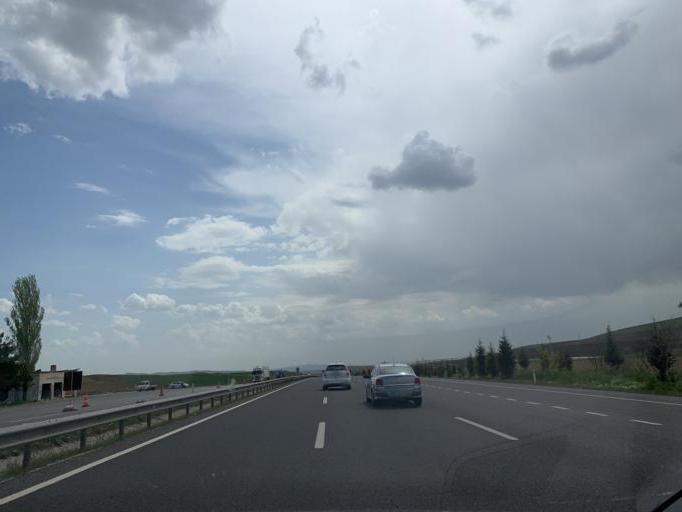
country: TR
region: Ankara
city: Polatli
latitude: 39.6155
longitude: 32.1867
